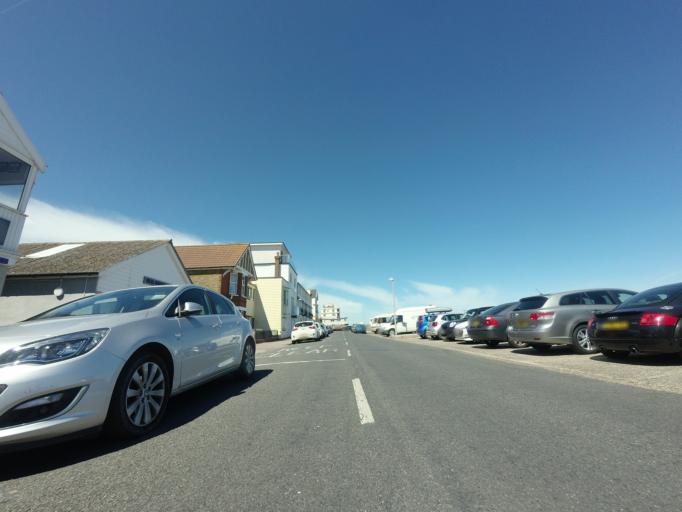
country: GB
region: England
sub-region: Kent
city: Deal
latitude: 51.2307
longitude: 1.4044
